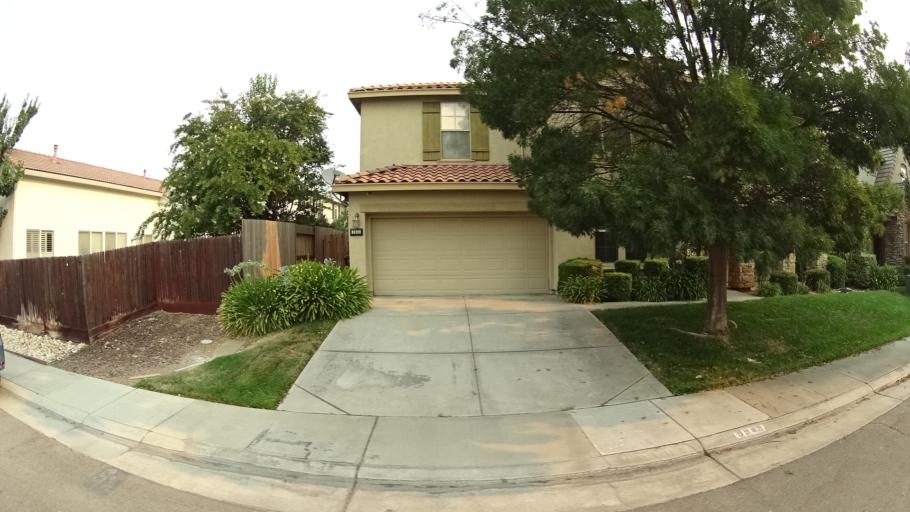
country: US
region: California
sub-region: Sacramento County
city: Laguna
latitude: 38.3971
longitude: -121.4423
